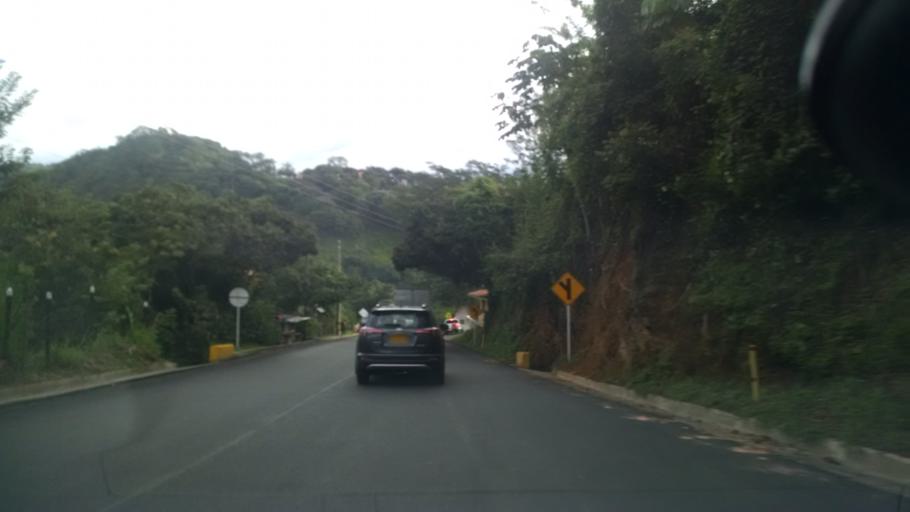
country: CO
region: Antioquia
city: Santa Barbara
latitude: 5.8520
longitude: -75.5742
